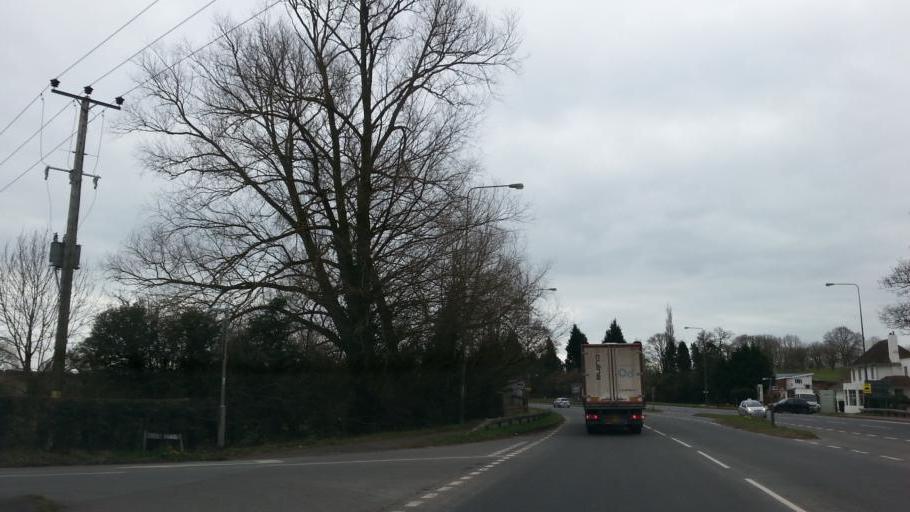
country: GB
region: England
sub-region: Staffordshire
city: Stone
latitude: 52.9047
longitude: -2.1611
